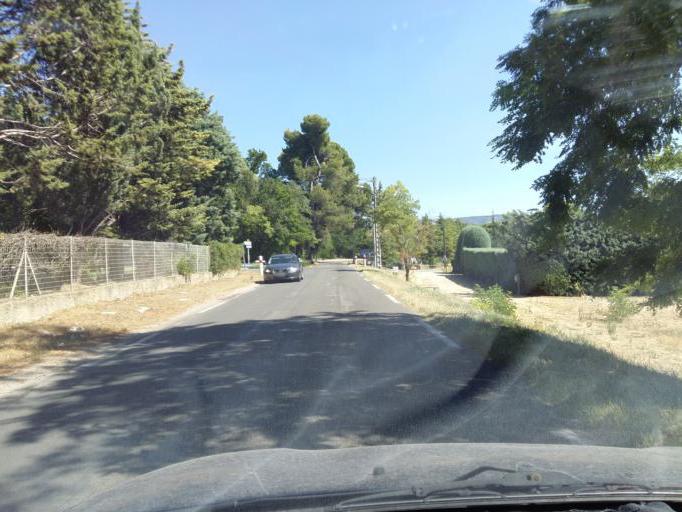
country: FR
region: Provence-Alpes-Cote d'Azur
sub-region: Departement du Vaucluse
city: Saint-Didier
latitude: 44.0162
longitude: 5.1011
